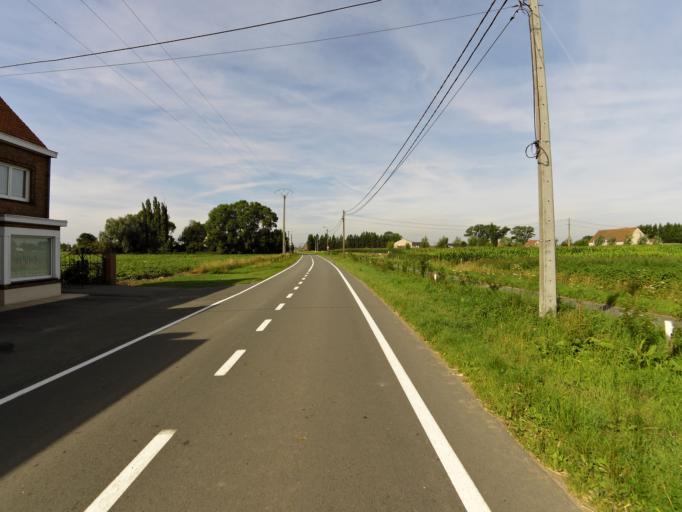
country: BE
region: Flanders
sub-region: Provincie West-Vlaanderen
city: Koekelare
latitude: 51.1129
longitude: 2.9352
